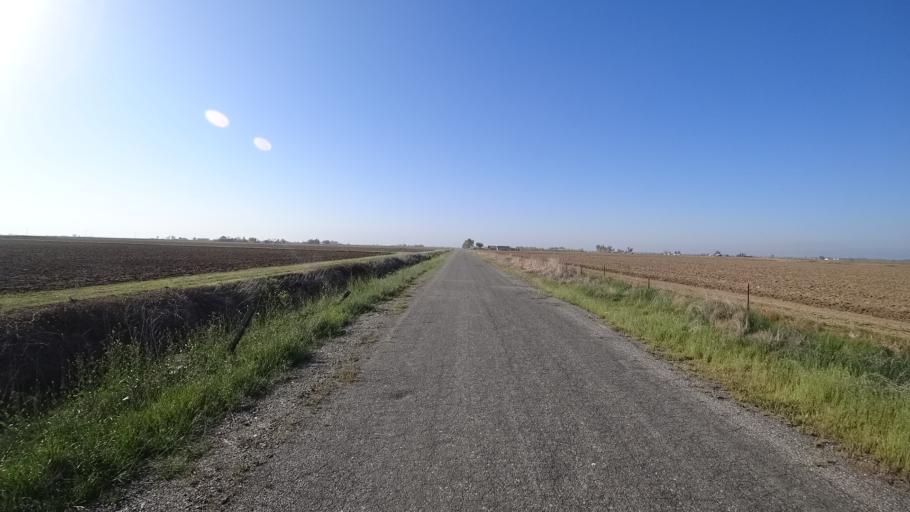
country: US
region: California
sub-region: Glenn County
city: Willows
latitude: 39.5524
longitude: -122.1321
